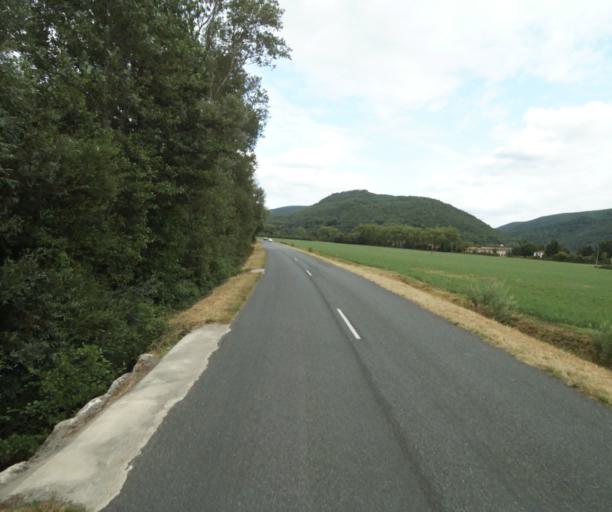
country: FR
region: Midi-Pyrenees
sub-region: Departement du Tarn
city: Soreze
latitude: 43.4529
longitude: 2.0558
